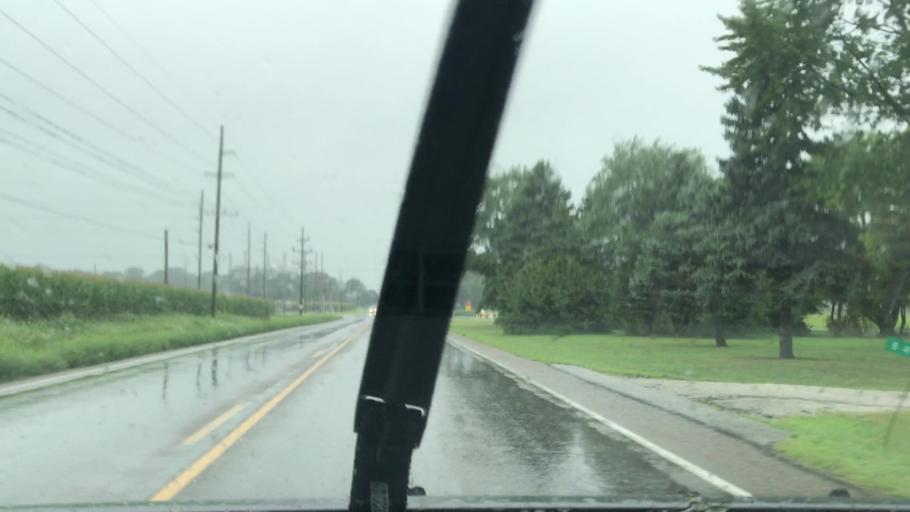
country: US
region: Indiana
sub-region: Hamilton County
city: Sheridan
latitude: 40.1144
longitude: -86.1740
